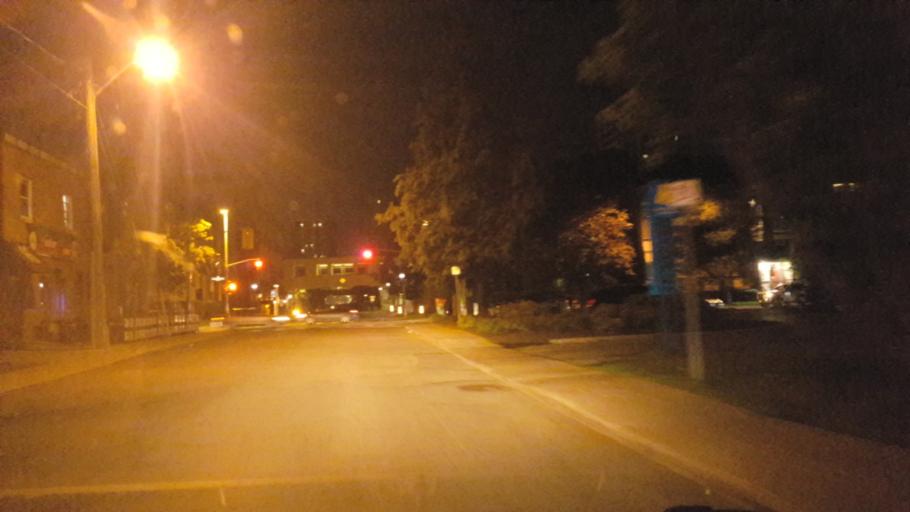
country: CA
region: Ontario
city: Ottawa
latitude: 45.4239
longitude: -75.6810
